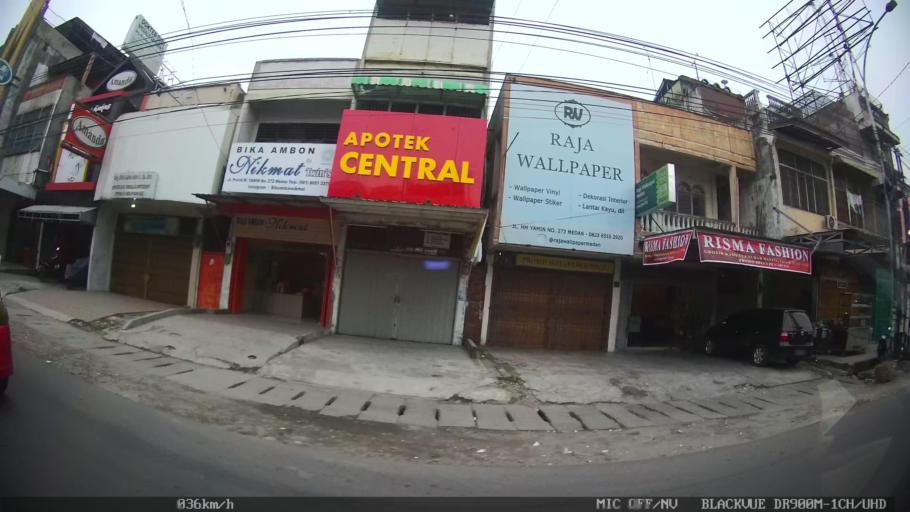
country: ID
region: North Sumatra
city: Medan
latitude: 3.5982
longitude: 98.7036
